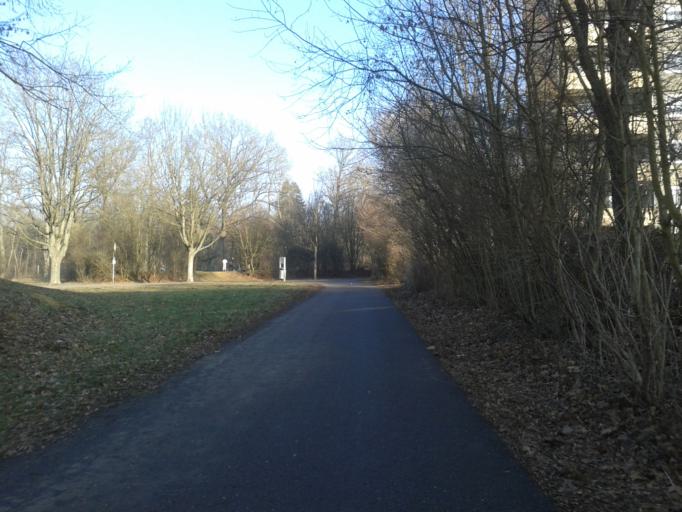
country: DE
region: Baden-Wuerttemberg
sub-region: Tuebingen Region
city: Ulm
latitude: 48.3623
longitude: 9.9765
